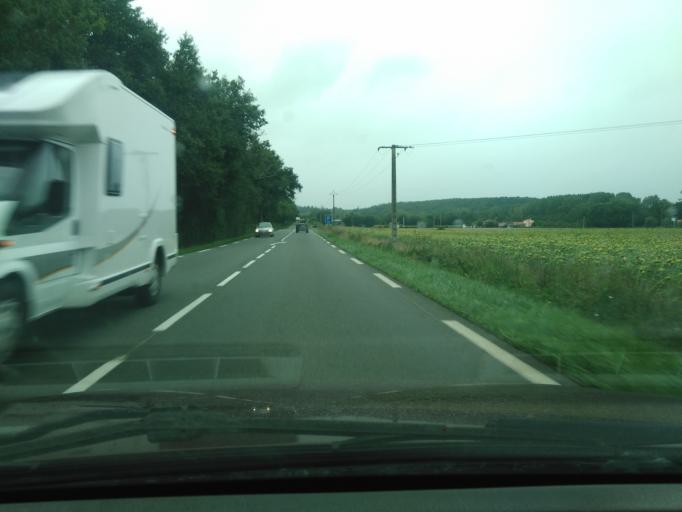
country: FR
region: Pays de la Loire
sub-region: Departement de la Vendee
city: Sainte-Hermine
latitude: 46.5819
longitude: -1.1118
